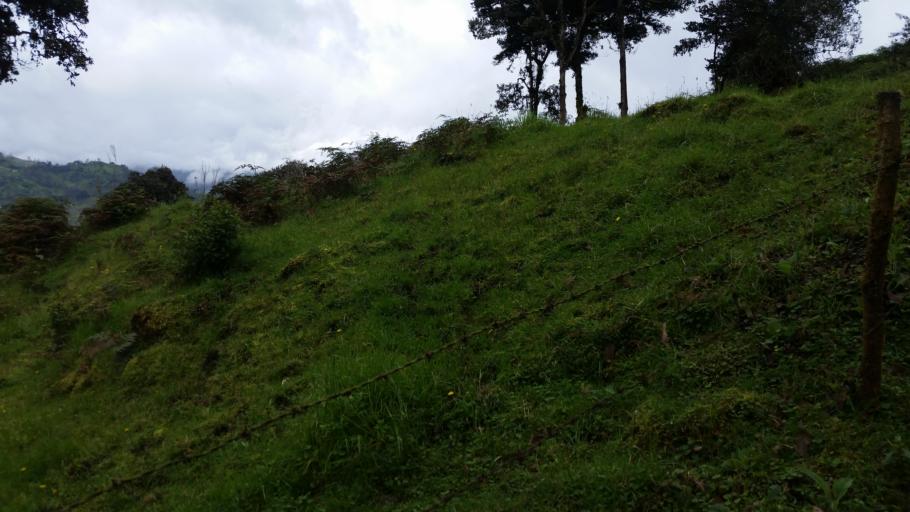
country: CO
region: Cundinamarca
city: Choachi
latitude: 4.5909
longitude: -73.9559
